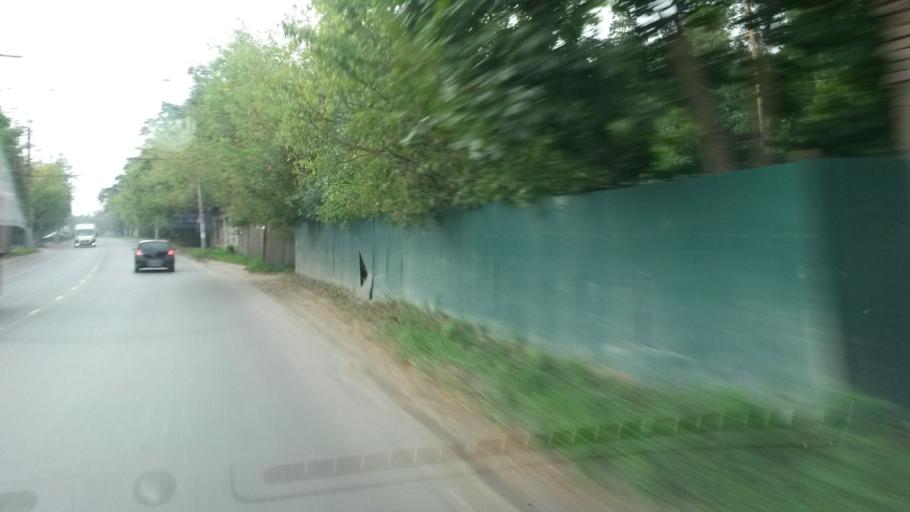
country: RU
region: Ivanovo
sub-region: Gorod Ivanovo
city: Ivanovo
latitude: 57.0234
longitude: 40.9444
